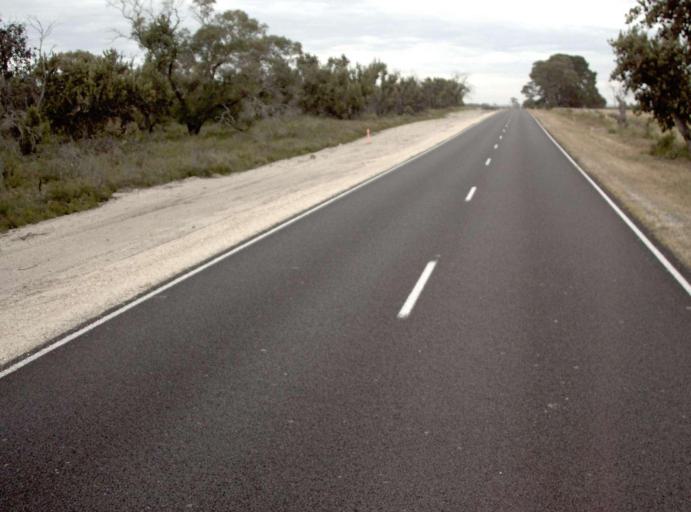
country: AU
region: Victoria
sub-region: Wellington
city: Sale
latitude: -38.1444
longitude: 147.3997
